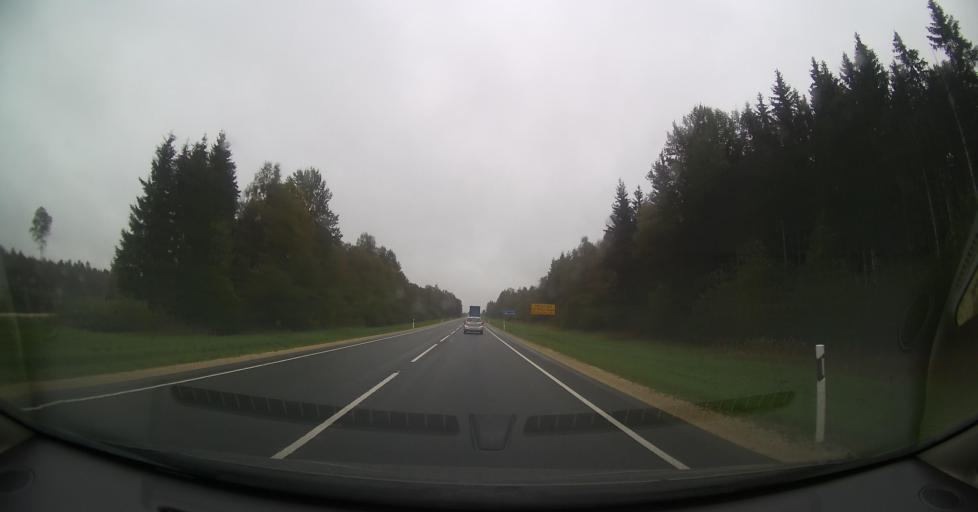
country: EE
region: Jogevamaa
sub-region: Poltsamaa linn
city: Poltsamaa
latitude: 58.7313
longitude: 25.8415
